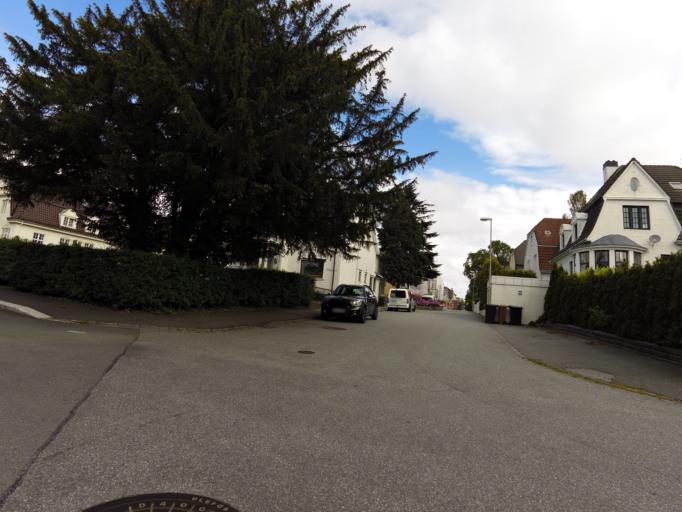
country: NO
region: Rogaland
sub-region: Stavanger
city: Stavanger
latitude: 58.9662
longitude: 5.7268
